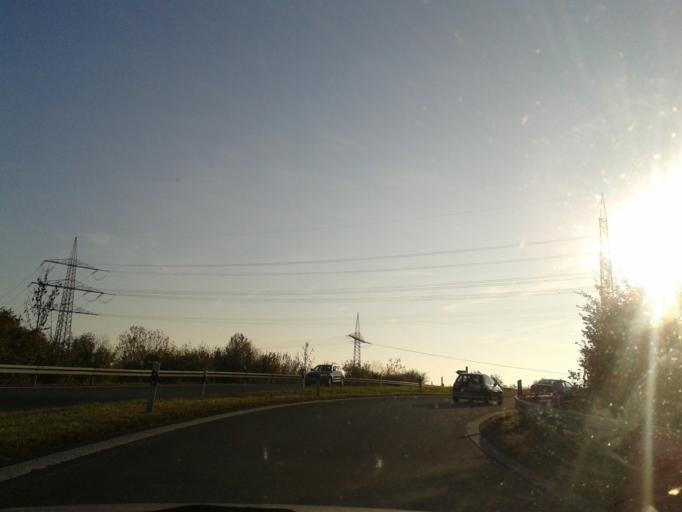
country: DE
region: North Rhine-Westphalia
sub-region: Regierungsbezirk Detmold
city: Paderborn
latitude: 51.7039
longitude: 8.7069
